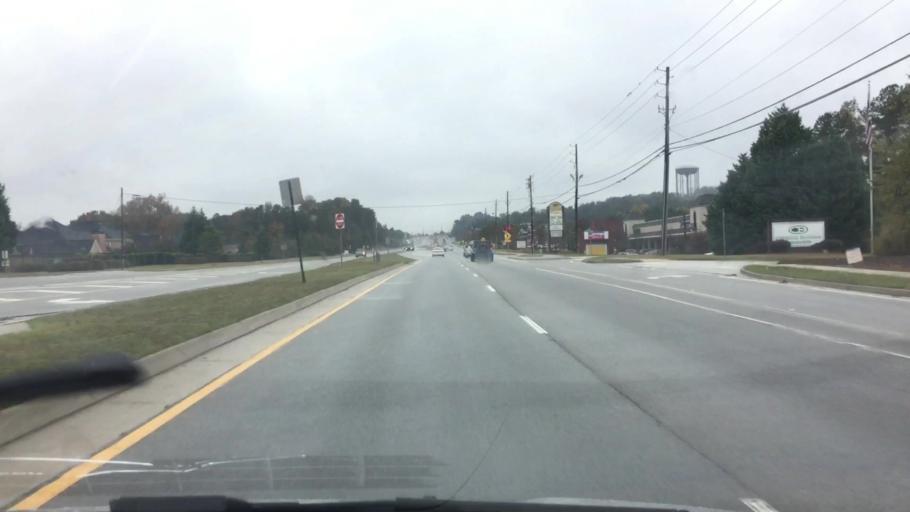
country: US
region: Georgia
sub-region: Henry County
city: Stockbridge
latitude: 33.5143
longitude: -84.2087
